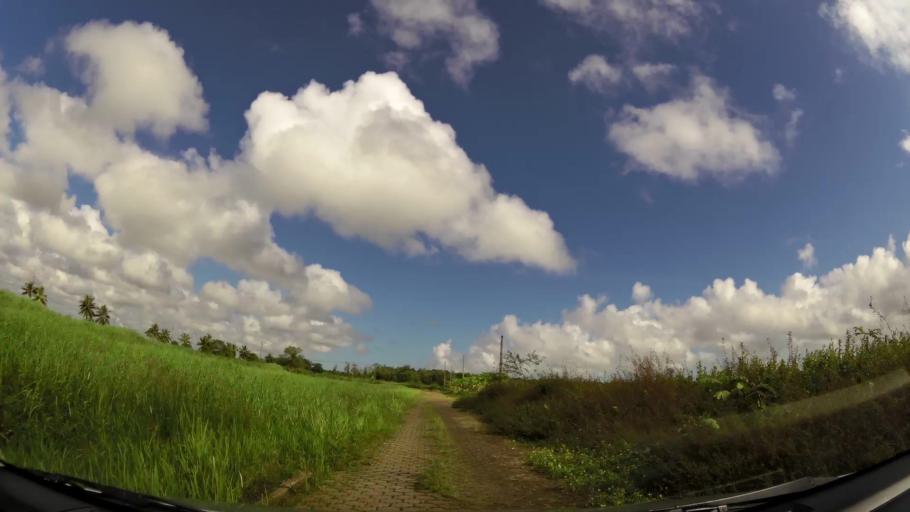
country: SR
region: Commewijne
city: Nieuw Amsterdam
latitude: 5.8802
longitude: -55.1154
